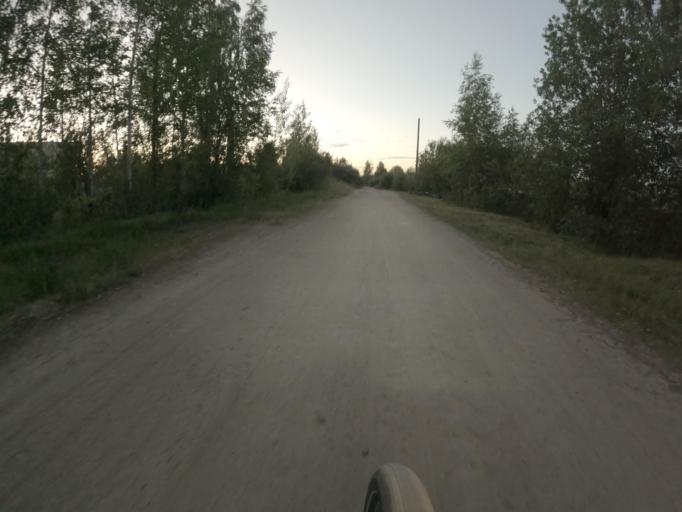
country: RU
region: St.-Petersburg
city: Sapernyy
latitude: 59.7803
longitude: 30.6726
